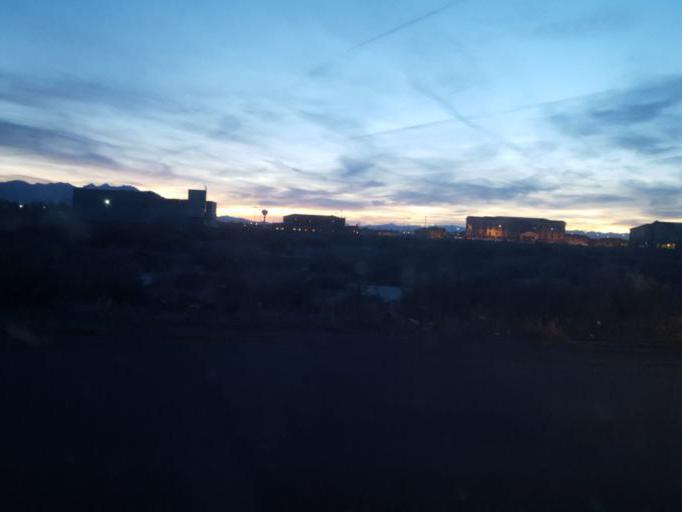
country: US
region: Colorado
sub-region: Alamosa County
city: Alamosa
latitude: 37.4839
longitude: -105.9121
